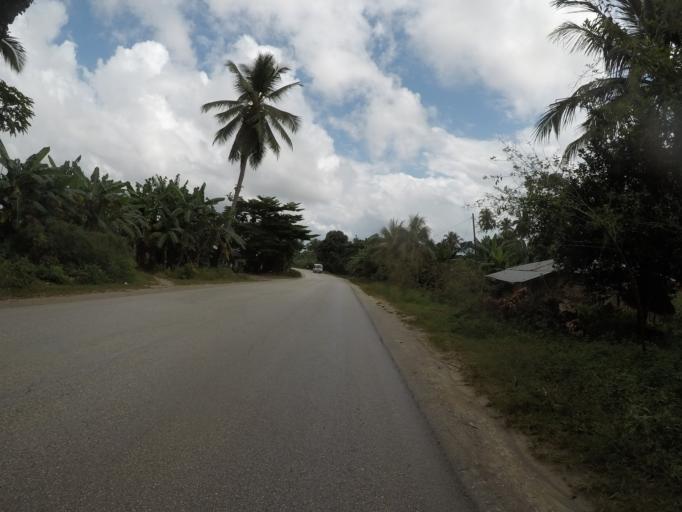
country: TZ
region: Zanzibar North
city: Gamba
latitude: -5.9677
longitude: 39.2527
